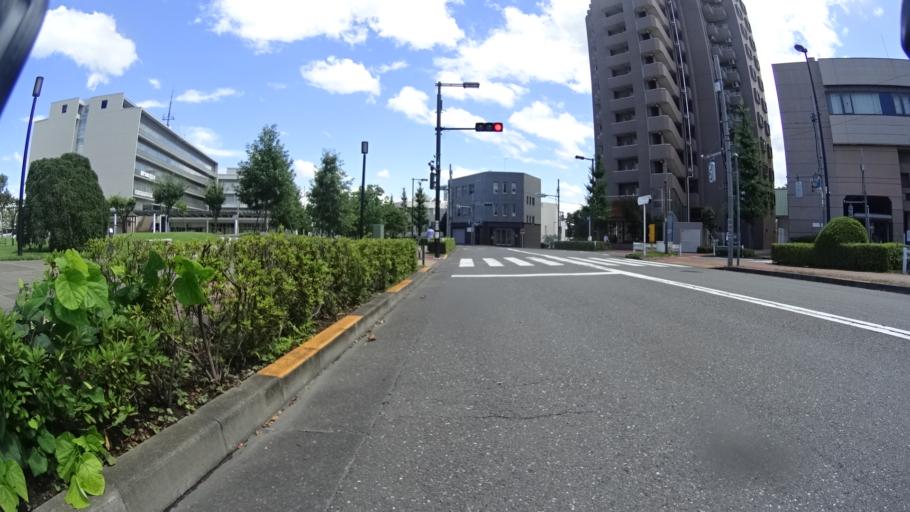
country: JP
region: Tokyo
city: Ome
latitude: 35.7881
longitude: 139.2743
